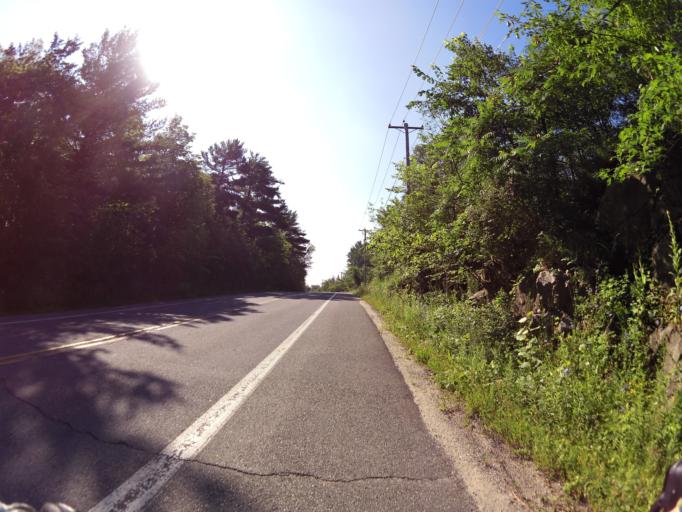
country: CA
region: Quebec
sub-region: Outaouais
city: Gatineau
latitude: 45.5114
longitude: -75.7926
